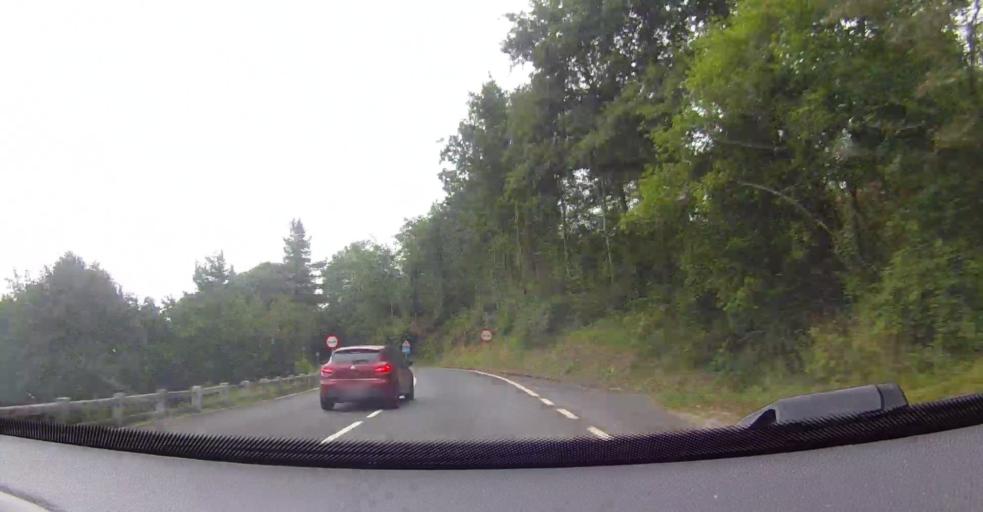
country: ES
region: Basque Country
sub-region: Bizkaia
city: Balmaseda
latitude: 43.2386
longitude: -3.2088
